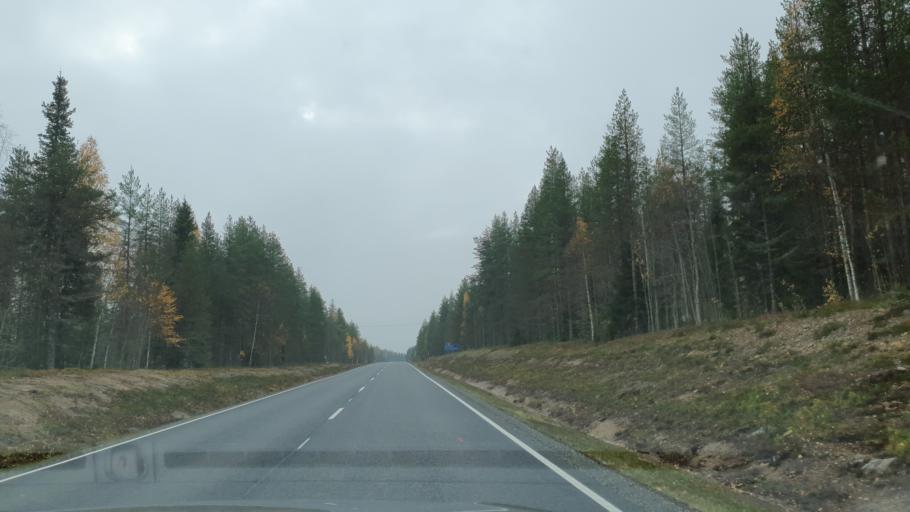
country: FI
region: Lapland
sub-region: Rovaniemi
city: Ranua
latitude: 66.0672
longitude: 26.3666
